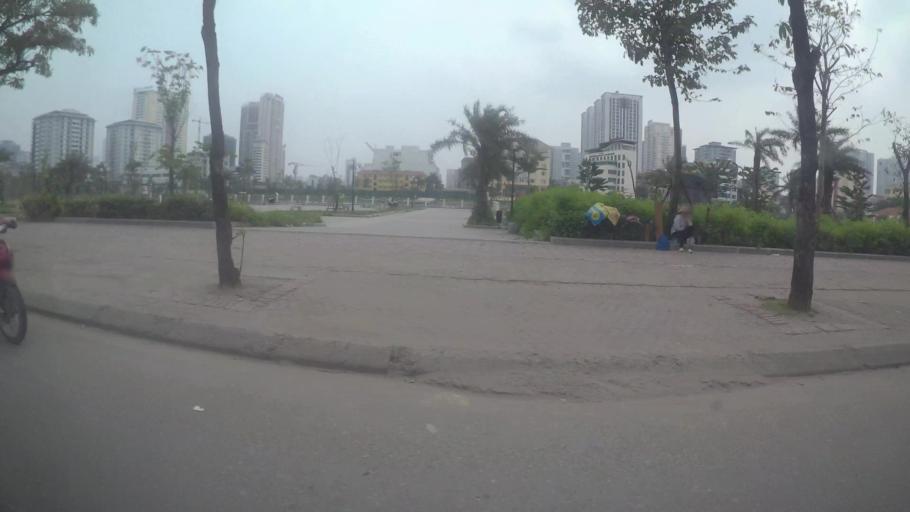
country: VN
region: Ha Noi
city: Cau Dien
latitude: 21.0388
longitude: 105.7693
